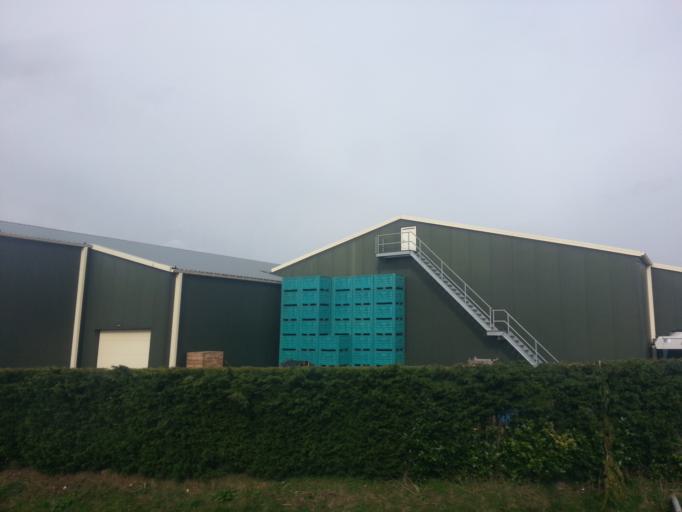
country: NL
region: Gelderland
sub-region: Gemeente Geldermalsen
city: Geldermalsen
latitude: 51.8702
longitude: 5.2712
